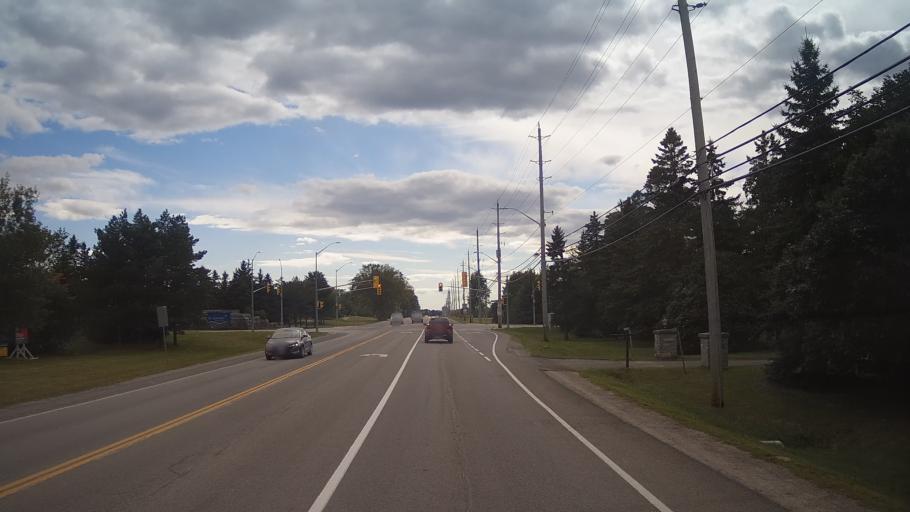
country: CA
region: Ontario
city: Kingston
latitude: 44.2736
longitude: -76.4462
